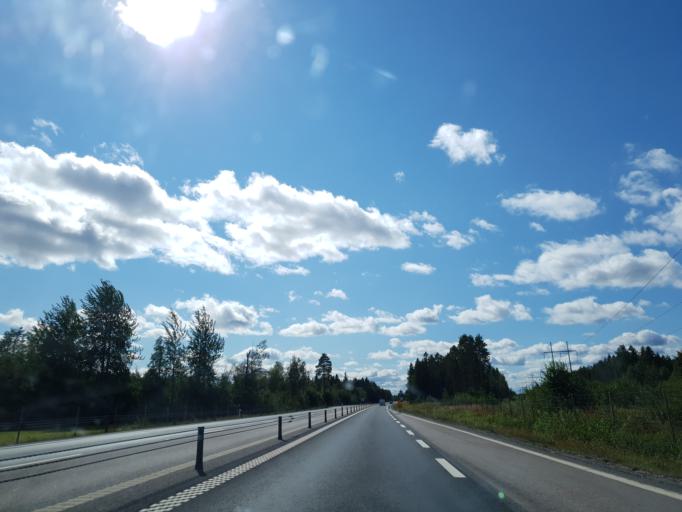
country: SE
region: Vaesterbotten
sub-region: Nordmalings Kommun
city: Nordmaling
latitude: 63.5333
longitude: 19.3984
